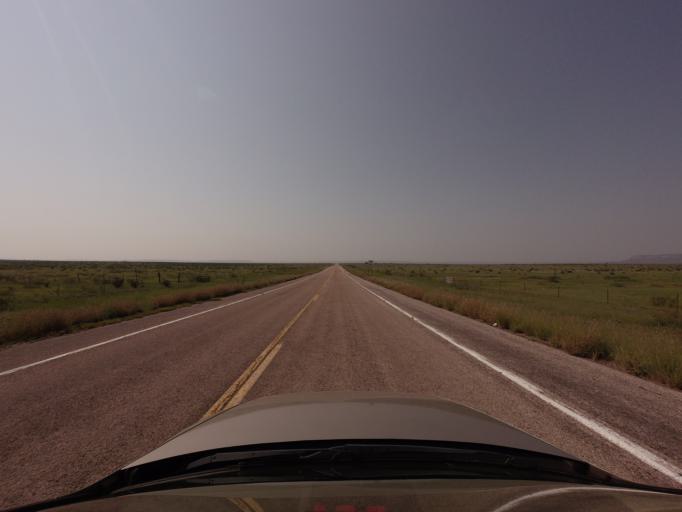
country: US
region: New Mexico
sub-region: Quay County
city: Tucumcari
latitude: 34.9655
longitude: -103.7549
